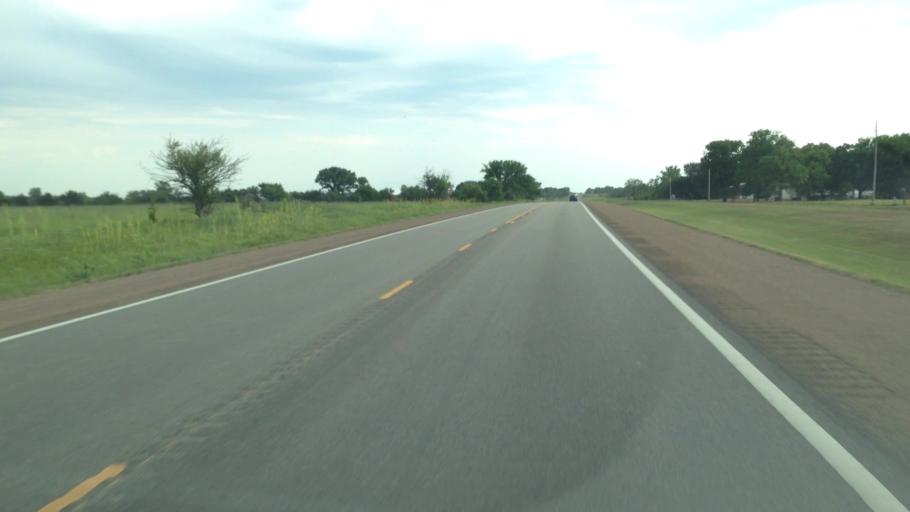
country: US
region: Kansas
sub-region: Woodson County
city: Yates Center
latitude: 38.0067
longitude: -95.7389
